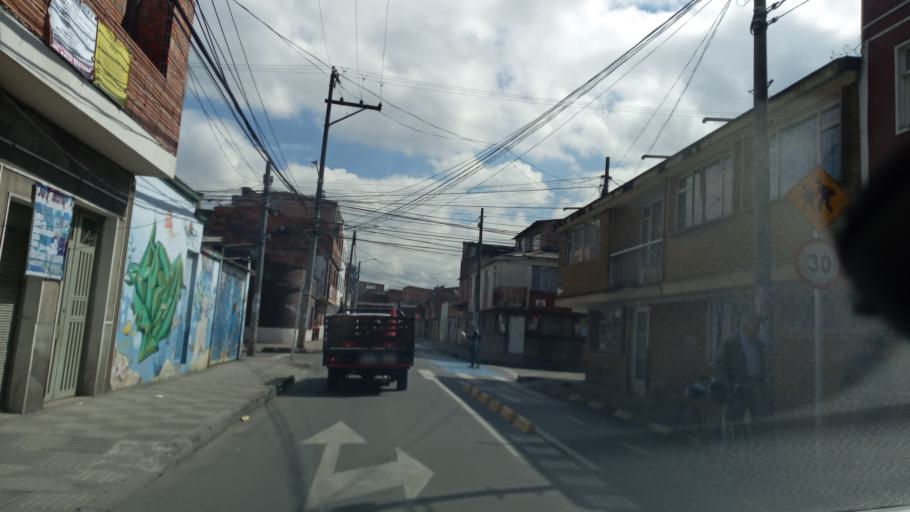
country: CO
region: Cundinamarca
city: Funza
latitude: 4.6801
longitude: -74.1402
